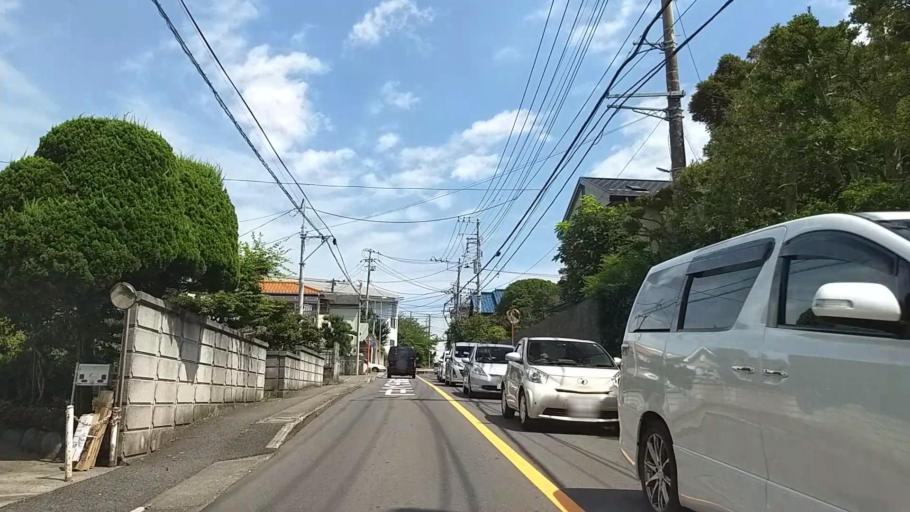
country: JP
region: Kanagawa
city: Fujisawa
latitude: 35.3500
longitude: 139.4578
